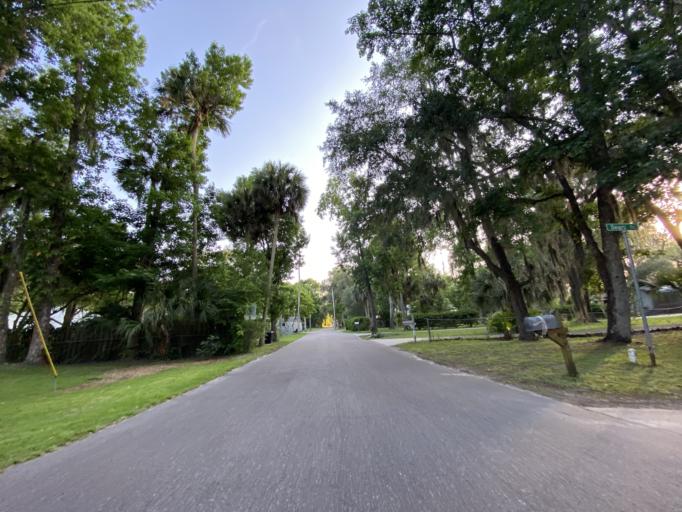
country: US
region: Florida
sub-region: Volusia County
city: Port Orange
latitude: 29.1452
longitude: -81.0048
